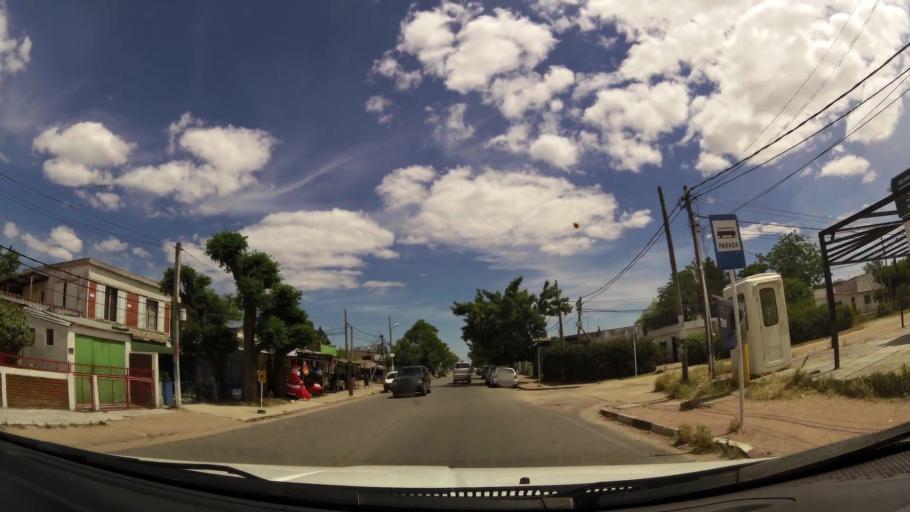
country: UY
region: San Jose
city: Delta del Tigre
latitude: -34.7466
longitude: -56.4534
